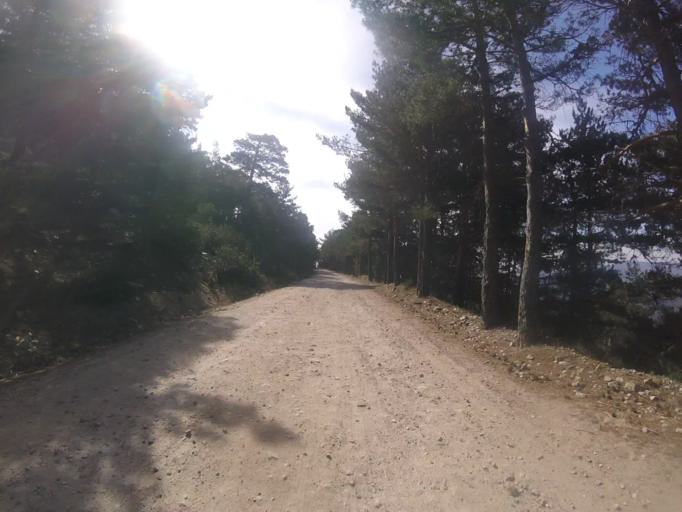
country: ES
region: Madrid
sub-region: Provincia de Madrid
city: Guadarrama
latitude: 40.6862
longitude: -4.1617
